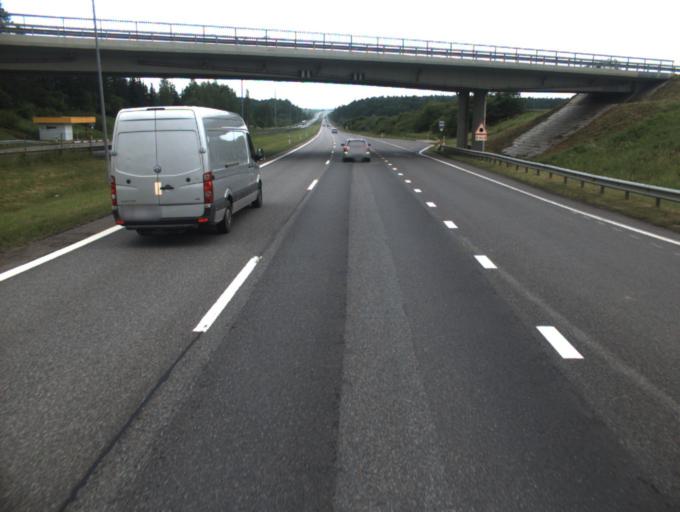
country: LT
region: Kauno apskritis
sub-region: Kaunas
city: Sargenai
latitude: 55.0962
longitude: 23.8025
